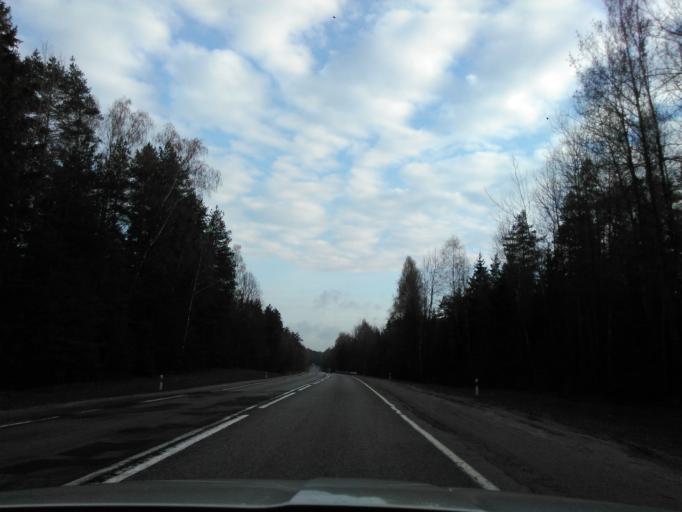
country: BY
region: Minsk
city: Plyeshchanitsy
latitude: 54.3191
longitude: 27.8753
